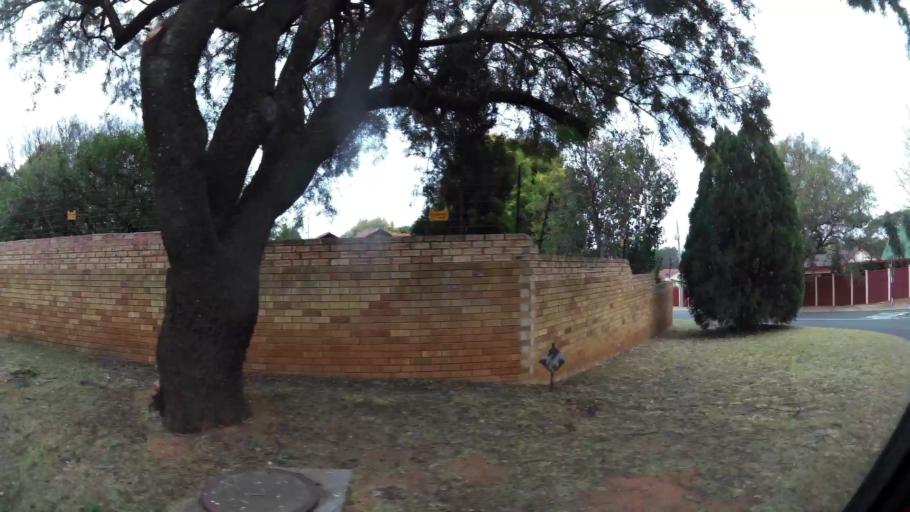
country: ZA
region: Gauteng
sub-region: City of Johannesburg Metropolitan Municipality
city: Roodepoort
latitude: -26.1228
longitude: 27.9058
